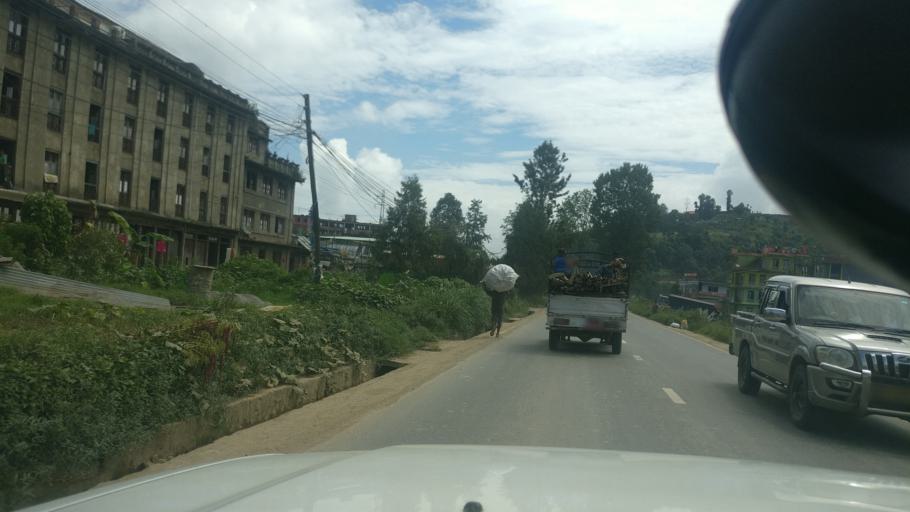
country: NP
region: Central Region
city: Banepa
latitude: 27.6322
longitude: 85.5040
